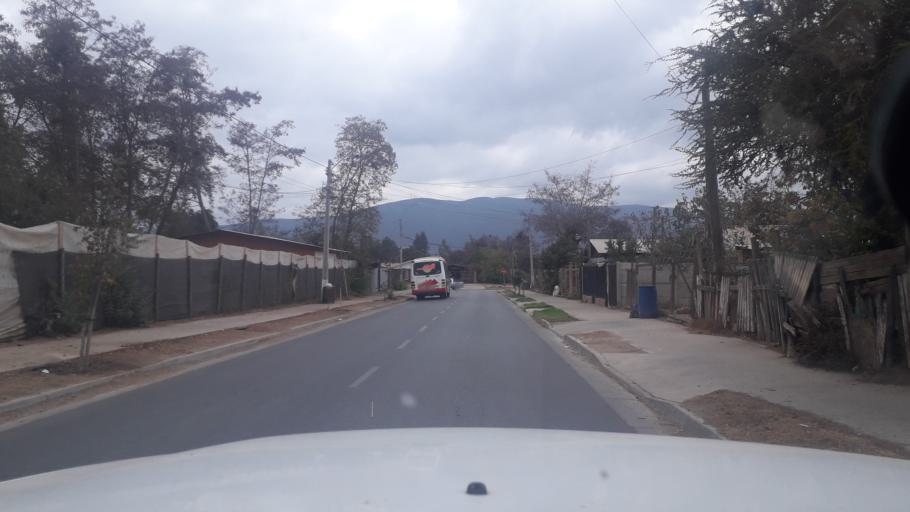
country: CL
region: Valparaiso
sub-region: Provincia de Marga Marga
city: Limache
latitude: -33.0156
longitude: -71.2680
